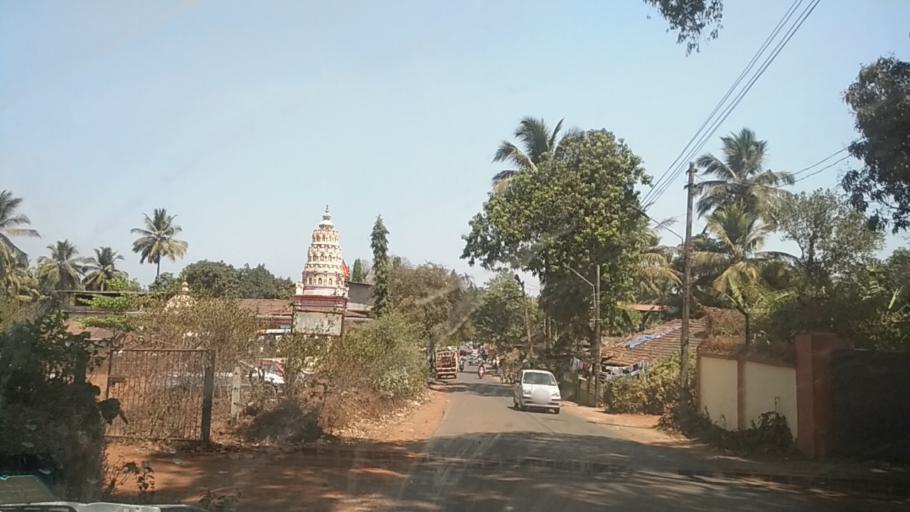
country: IN
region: Goa
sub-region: North Goa
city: Dicholi
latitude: 15.5865
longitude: 73.9434
